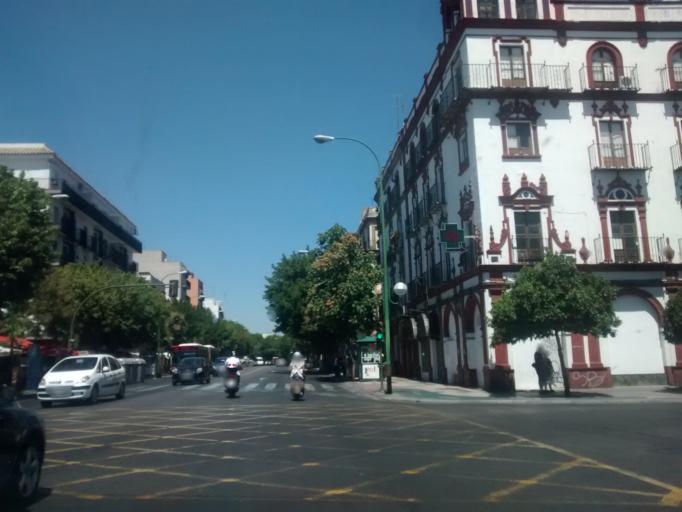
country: ES
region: Andalusia
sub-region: Provincia de Sevilla
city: Sevilla
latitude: 37.3856
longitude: -5.9861
